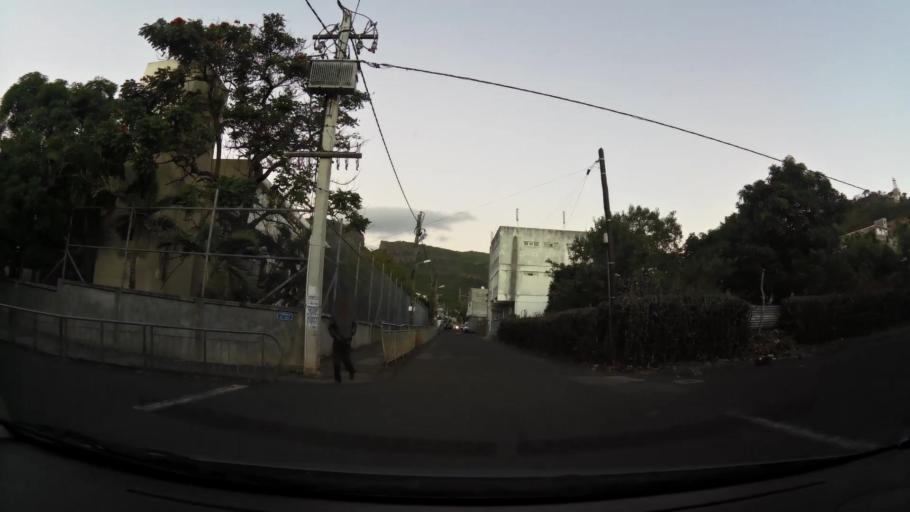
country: MU
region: Port Louis
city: Port Louis
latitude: -20.1679
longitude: 57.5166
